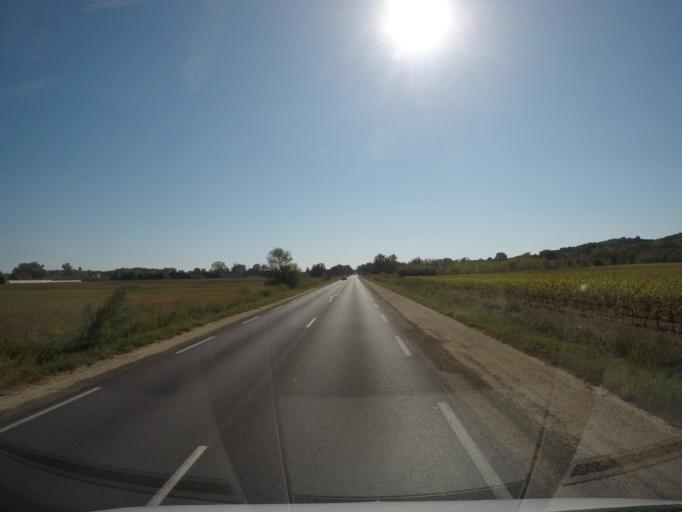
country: FR
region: Languedoc-Roussillon
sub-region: Departement du Gard
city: Moussac
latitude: 43.9810
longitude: 4.2033
